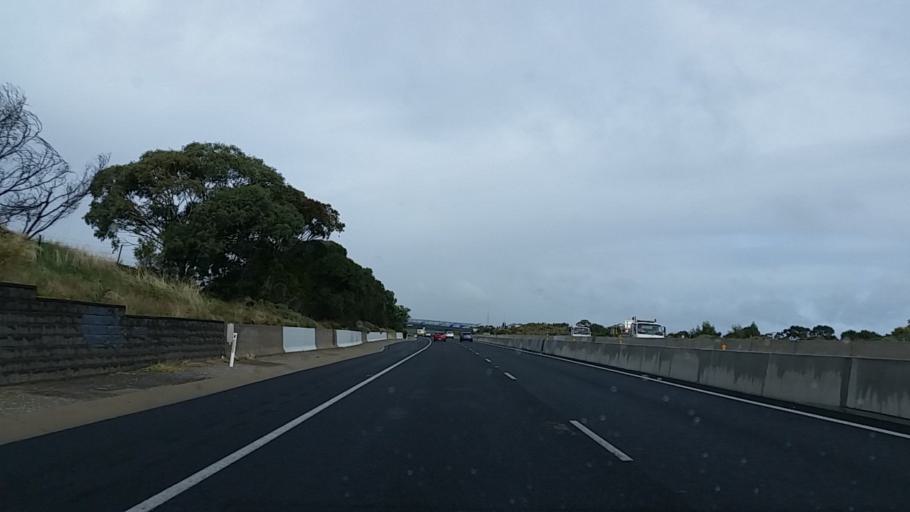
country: AU
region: South Australia
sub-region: Onkaparinga
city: Noarlunga Downs
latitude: -35.1539
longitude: 138.5060
